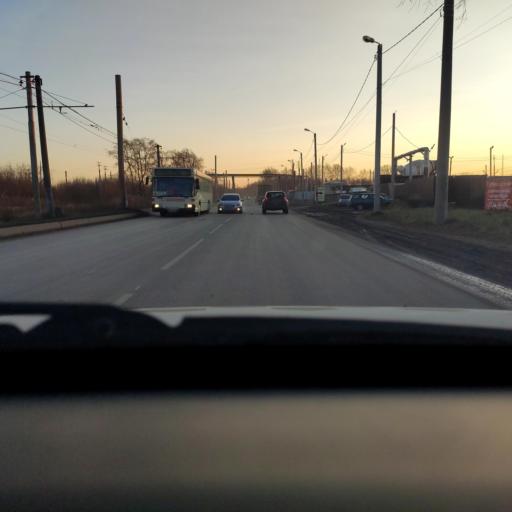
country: RU
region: Perm
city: Kondratovo
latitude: 57.9427
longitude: 56.1258
